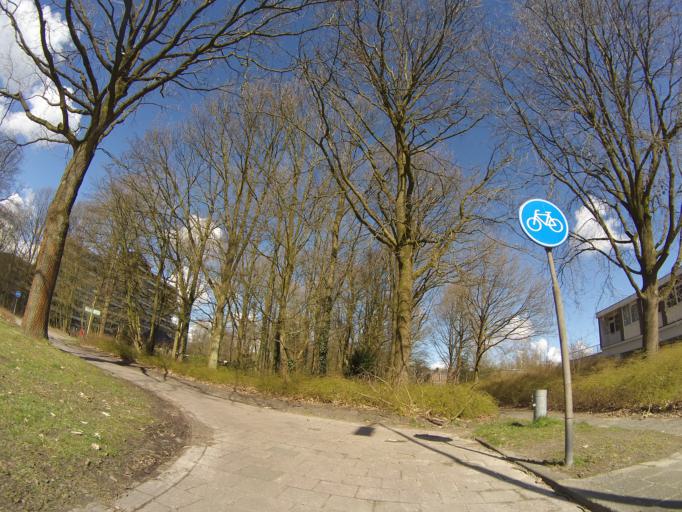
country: NL
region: Drenthe
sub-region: Gemeente Emmen
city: Emmen
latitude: 52.7790
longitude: 6.9174
